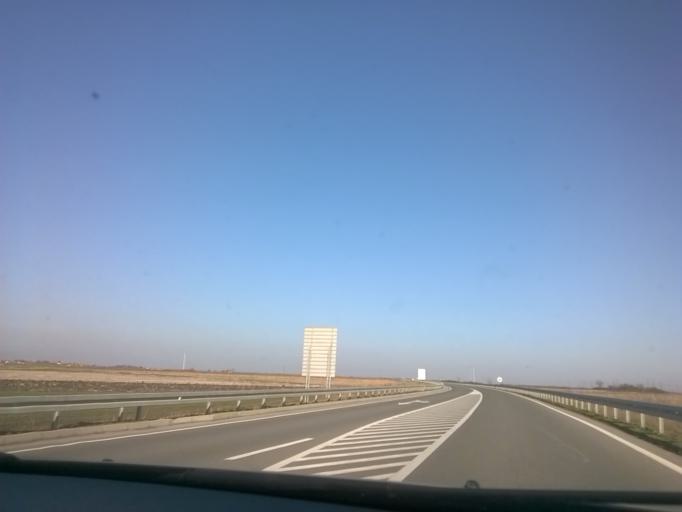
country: RS
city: Pavlis
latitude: 45.0959
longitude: 21.2610
